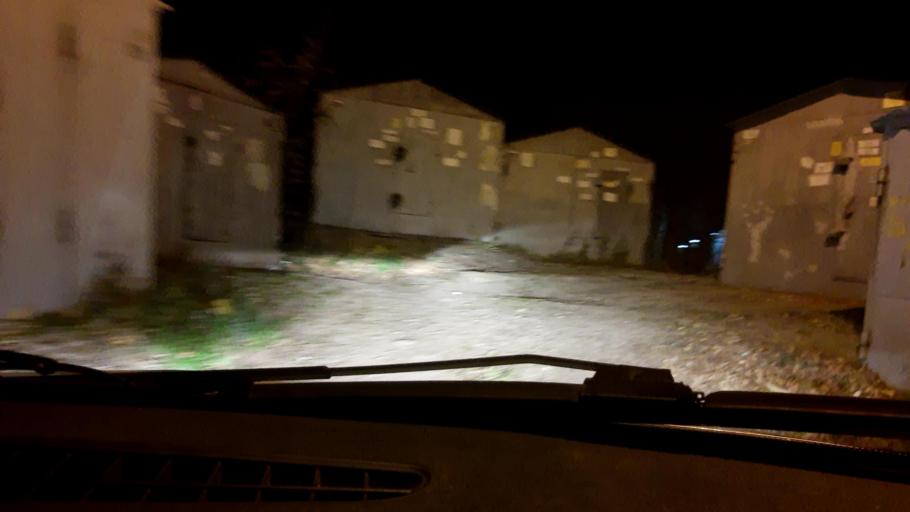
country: RU
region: Bashkortostan
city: Ufa
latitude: 54.7660
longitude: 56.0001
